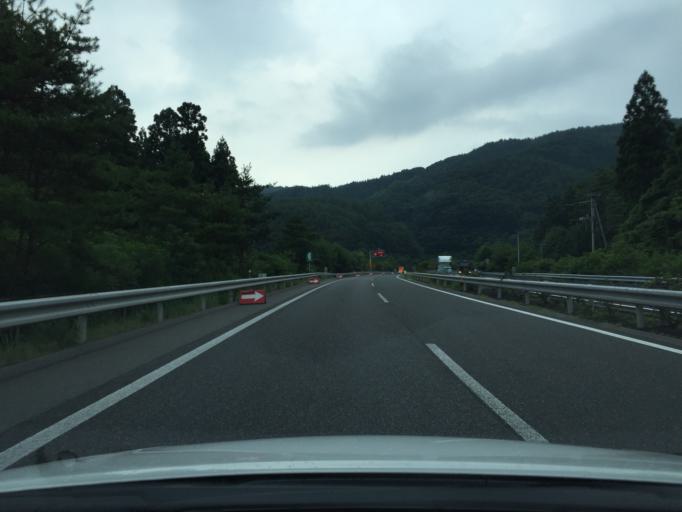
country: JP
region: Fukushima
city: Iwaki
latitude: 37.1311
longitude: 140.7539
